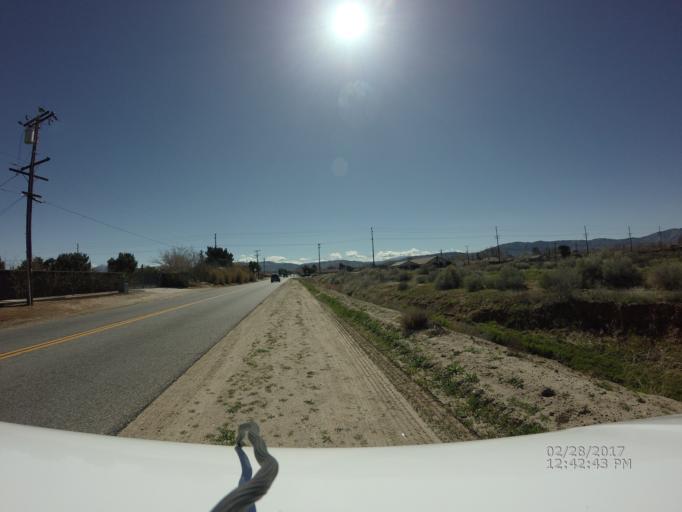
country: US
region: California
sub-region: Los Angeles County
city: Palmdale
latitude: 34.5886
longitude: -118.0853
